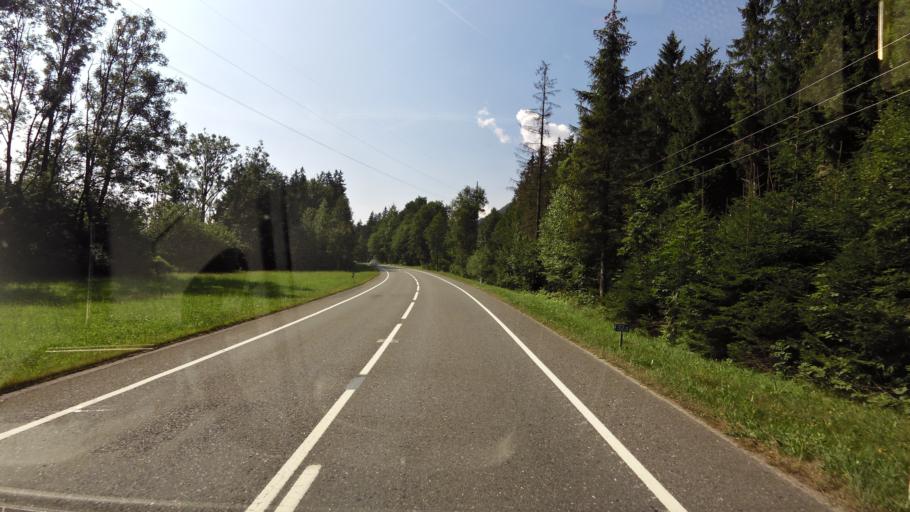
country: AT
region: Salzburg
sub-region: Politischer Bezirk Sankt Johann im Pongau
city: Werfen
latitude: 47.5173
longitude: 13.1640
